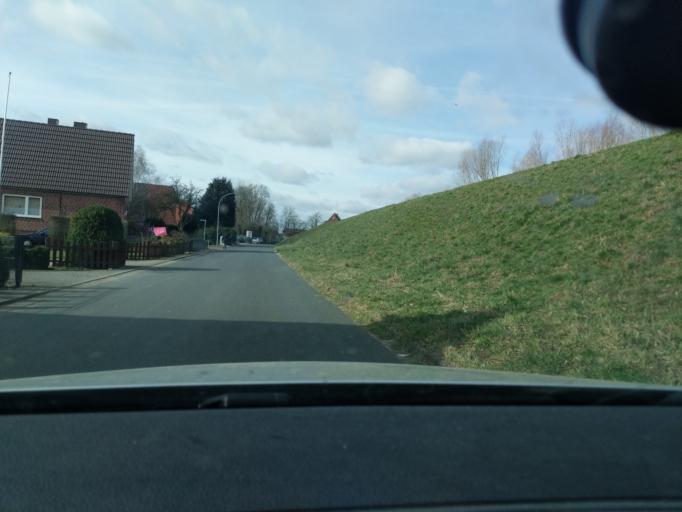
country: DE
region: Lower Saxony
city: Drochtersen
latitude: 53.7166
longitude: 9.3840
